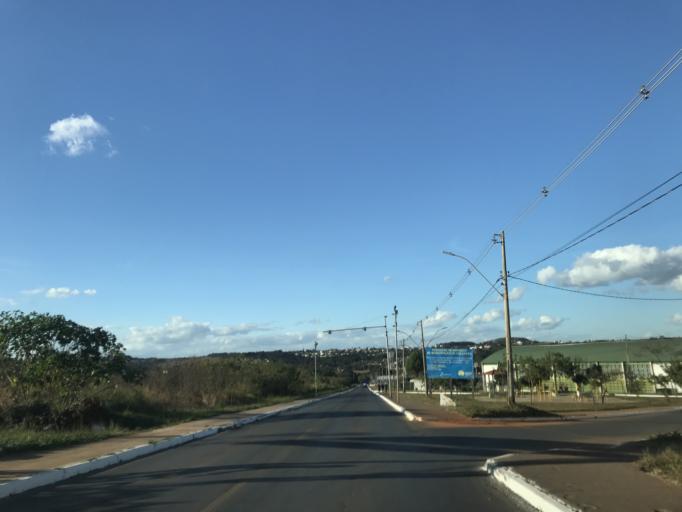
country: BR
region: Federal District
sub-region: Brasilia
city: Brasilia
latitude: -15.8926
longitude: -47.7833
